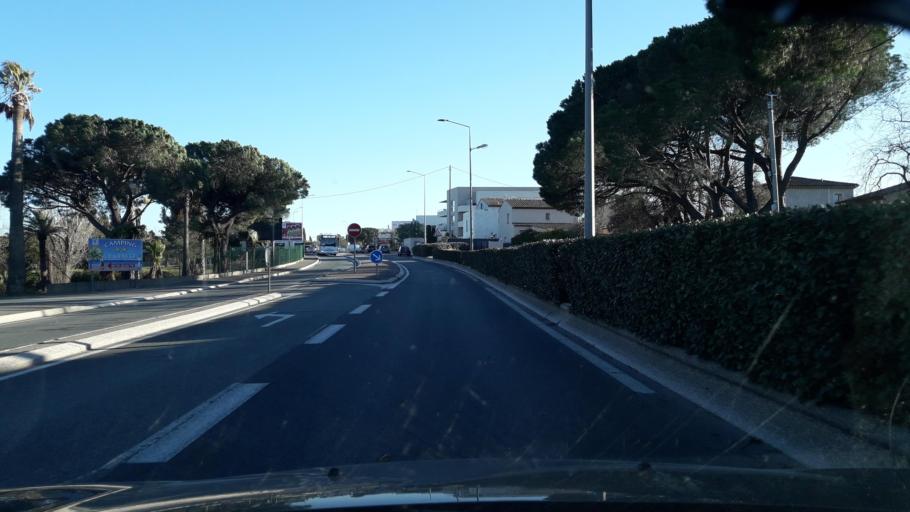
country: FR
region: Provence-Alpes-Cote d'Azur
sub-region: Departement du Var
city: Frejus
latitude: 43.4519
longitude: 6.7266
